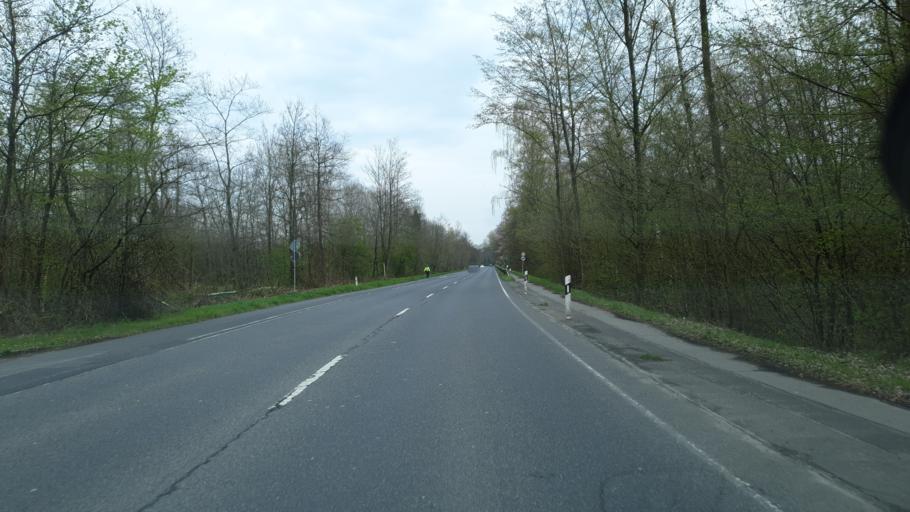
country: DE
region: North Rhine-Westphalia
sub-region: Regierungsbezirk Koln
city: Frechen
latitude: 50.9050
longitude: 6.7791
